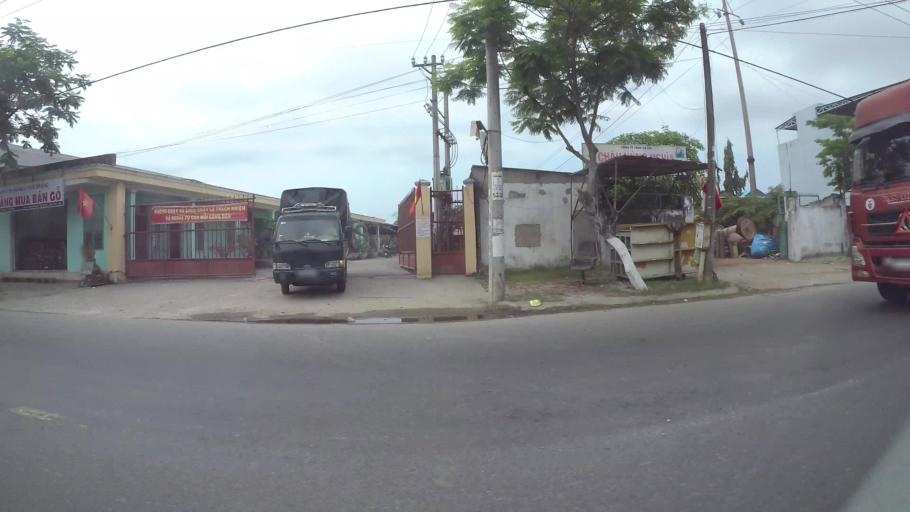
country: VN
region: Da Nang
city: Cam Le
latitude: 16.0352
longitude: 108.1808
